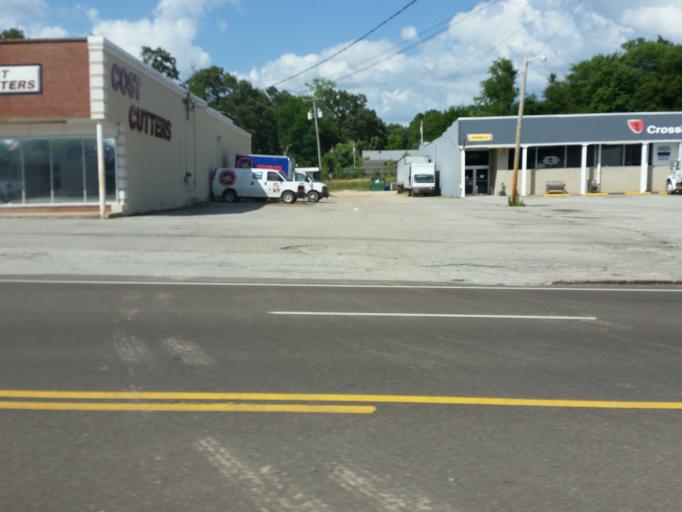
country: US
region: Tennessee
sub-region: Henderson County
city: Lexington
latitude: 35.6525
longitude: -88.3954
